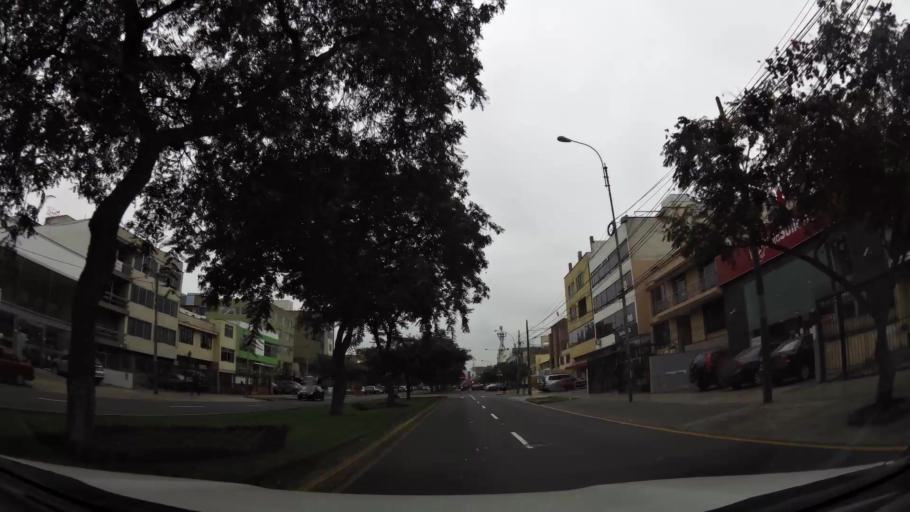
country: PE
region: Lima
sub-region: Lima
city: San Luis
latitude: -12.0920
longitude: -76.9959
